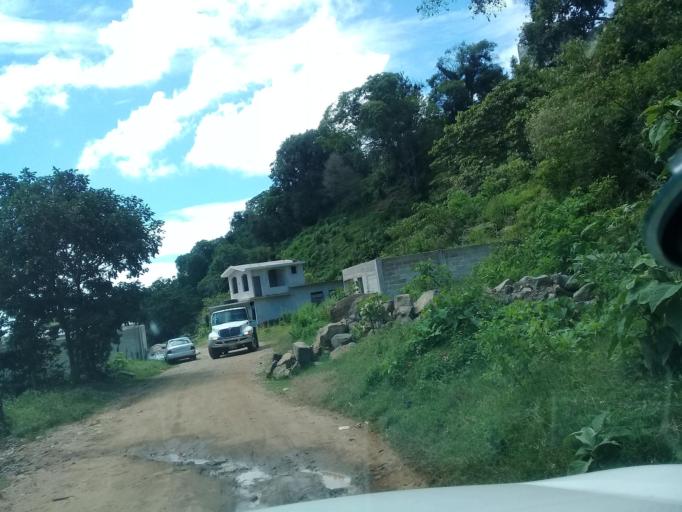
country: MX
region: Veracruz
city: El Castillo
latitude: 19.5715
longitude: -96.8892
